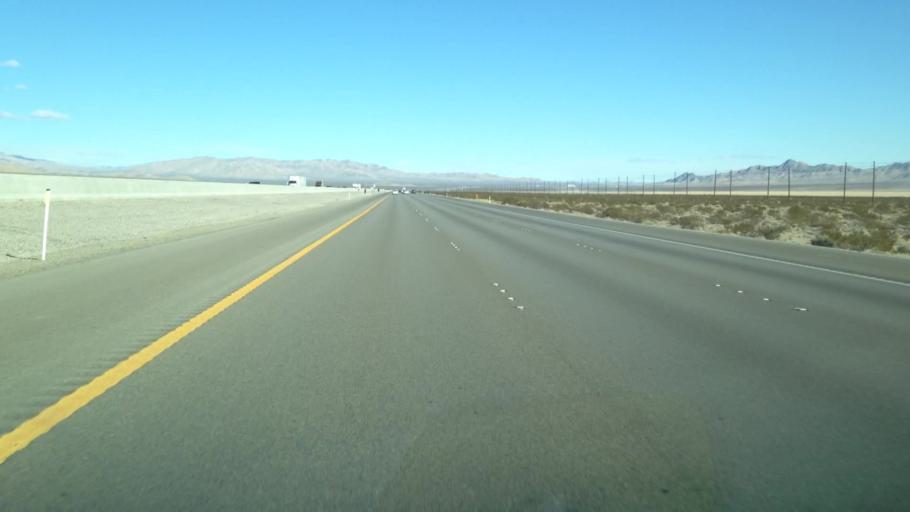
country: US
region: Nevada
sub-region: Clark County
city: Sandy Valley
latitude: 35.6375
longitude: -115.3840
